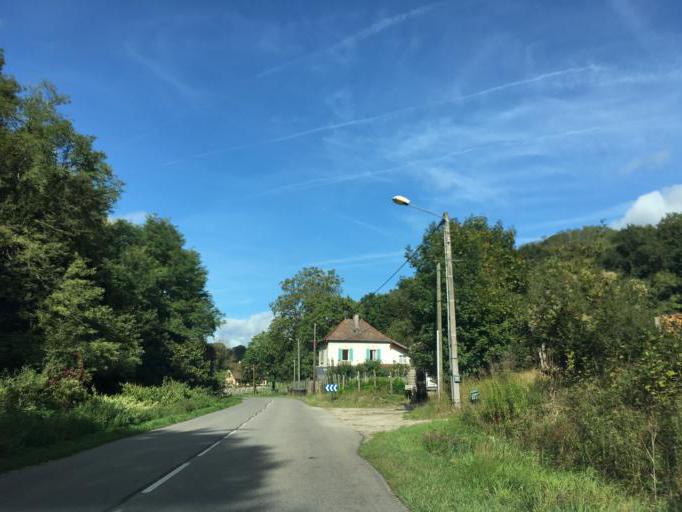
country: FR
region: Rhone-Alpes
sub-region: Departement de l'Isere
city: Saint-Clair-de-la-Tour
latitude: 45.5678
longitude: 5.4780
